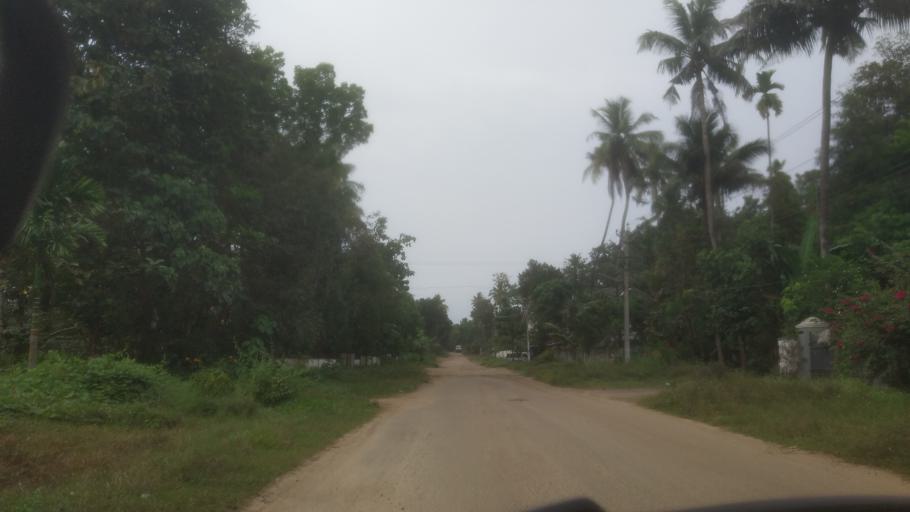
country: IN
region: Kerala
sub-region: Ernakulam
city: Perumbavoor
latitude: 10.0524
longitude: 76.5213
